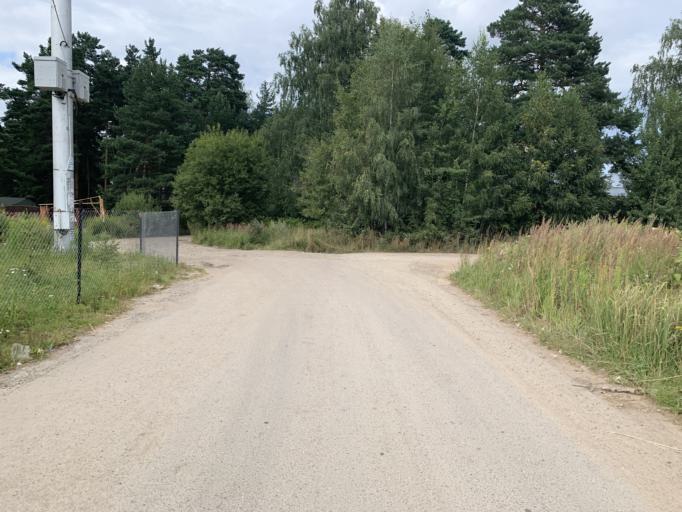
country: RU
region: Moskovskaya
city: Cherkizovo
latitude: 55.9903
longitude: 37.8012
